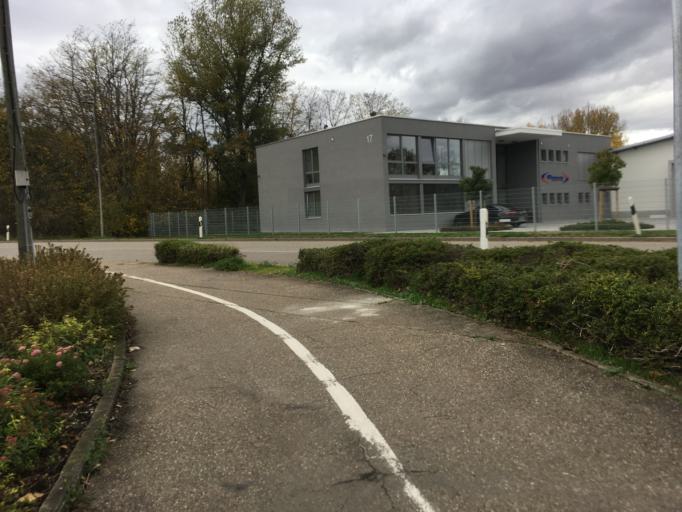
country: DE
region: Baden-Wuerttemberg
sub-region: Freiburg Region
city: Breisach am Rhein
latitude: 48.0438
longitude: 7.5757
